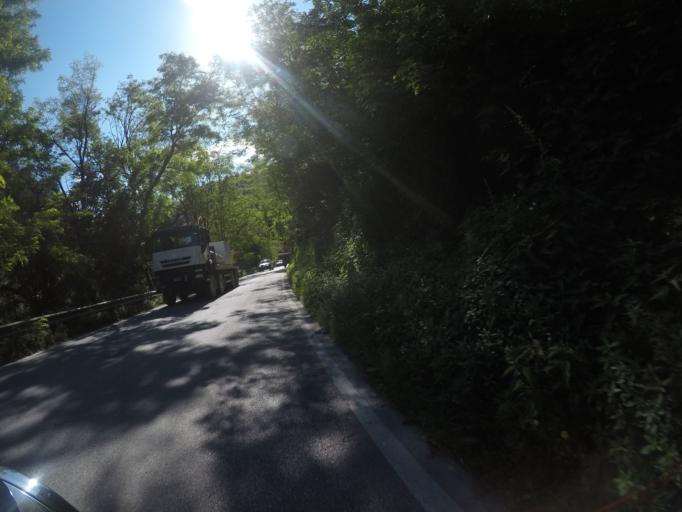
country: IT
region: Tuscany
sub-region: Provincia di Massa-Carrara
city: Montignoso
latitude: 44.0460
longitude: 10.1507
